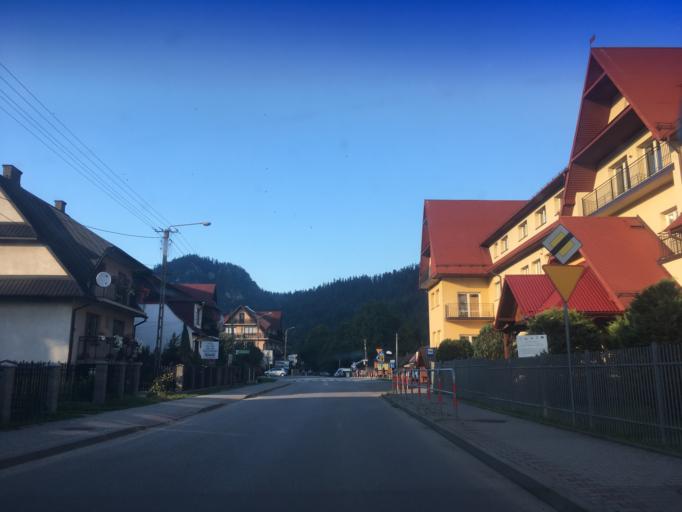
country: PL
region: Lesser Poland Voivodeship
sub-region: Powiat nowotarski
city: Kroscienko nad Dunajcem
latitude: 49.3946
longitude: 20.4085
